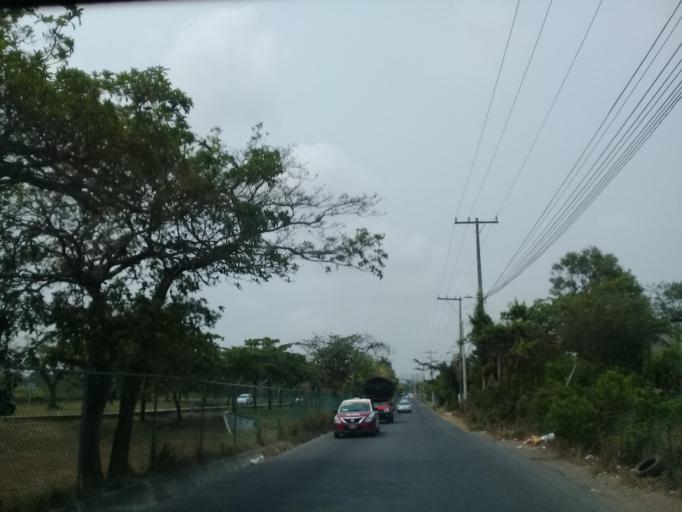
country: MX
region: Veracruz
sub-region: Veracruz
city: Hacienda Sotavento
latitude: 19.1426
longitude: -96.1768
